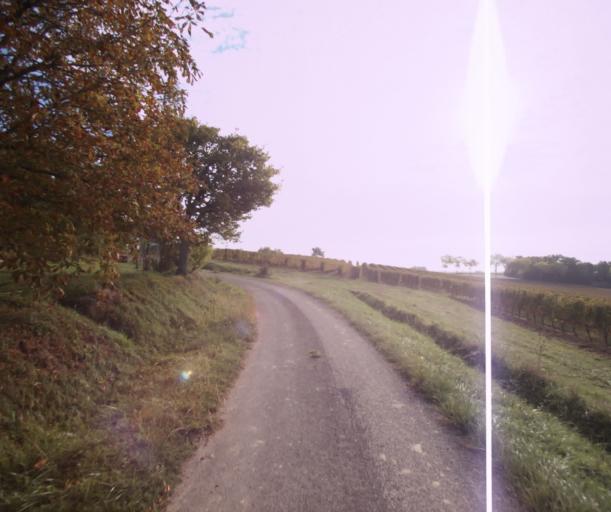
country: FR
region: Midi-Pyrenees
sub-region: Departement du Gers
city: Eauze
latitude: 43.8946
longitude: 0.0282
